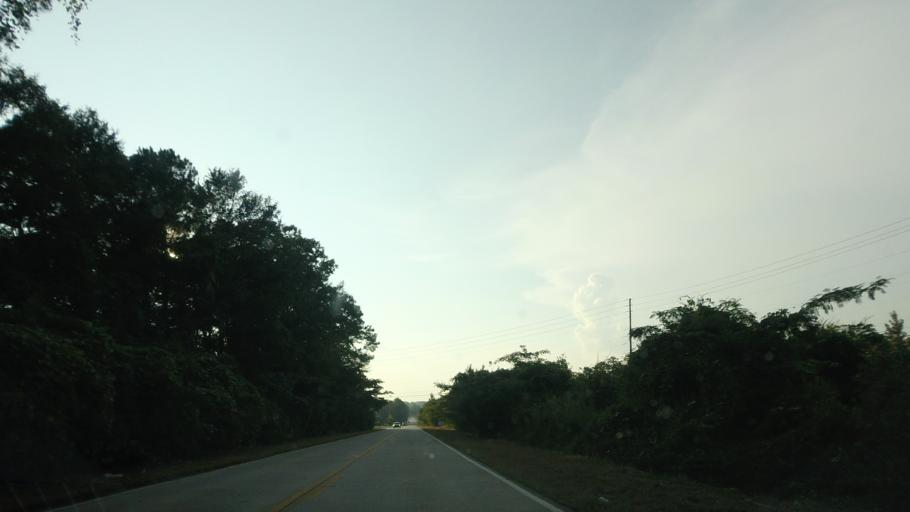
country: US
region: Georgia
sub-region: Bibb County
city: Macon
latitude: 32.9332
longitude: -83.7199
